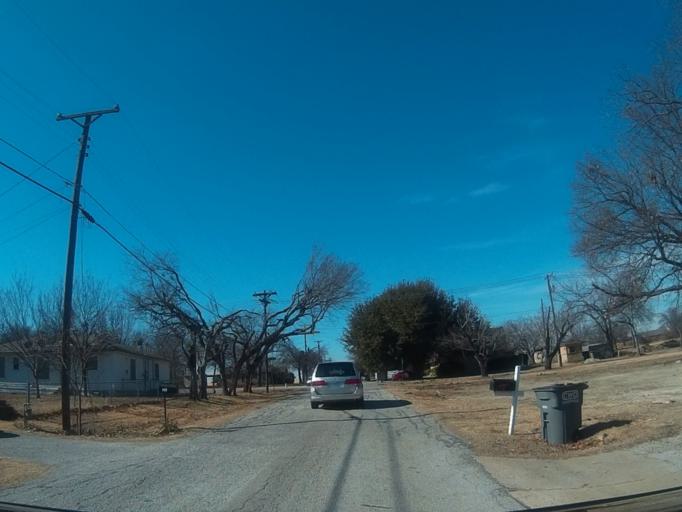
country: US
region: Texas
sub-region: Collin County
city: Allen
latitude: 33.1043
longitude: -96.6742
